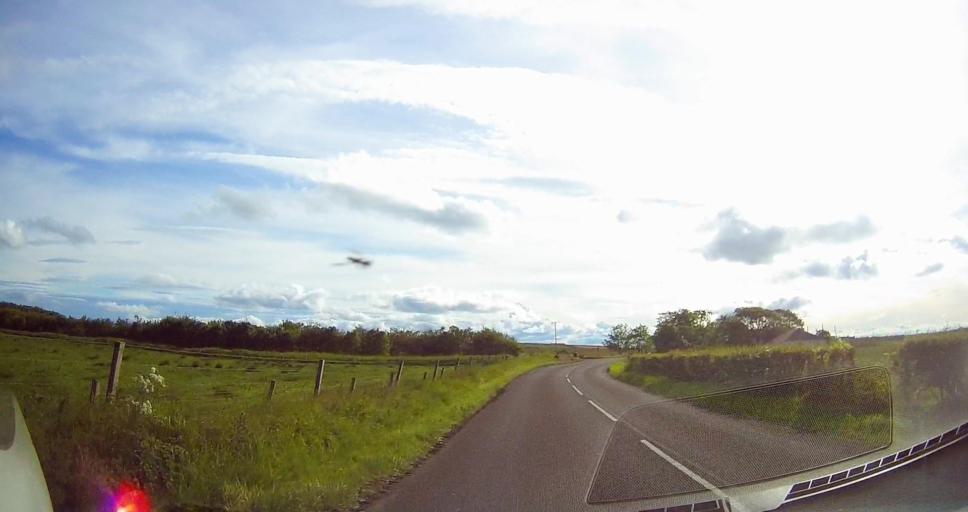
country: GB
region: Scotland
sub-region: Highland
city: Thurso
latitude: 58.6297
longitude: -3.3030
